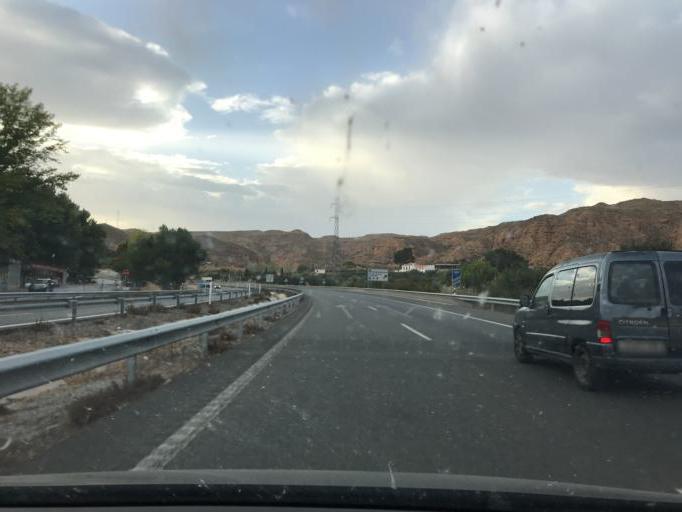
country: ES
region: Andalusia
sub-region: Provincia de Granada
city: Purullena
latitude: 37.3301
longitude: -3.2181
